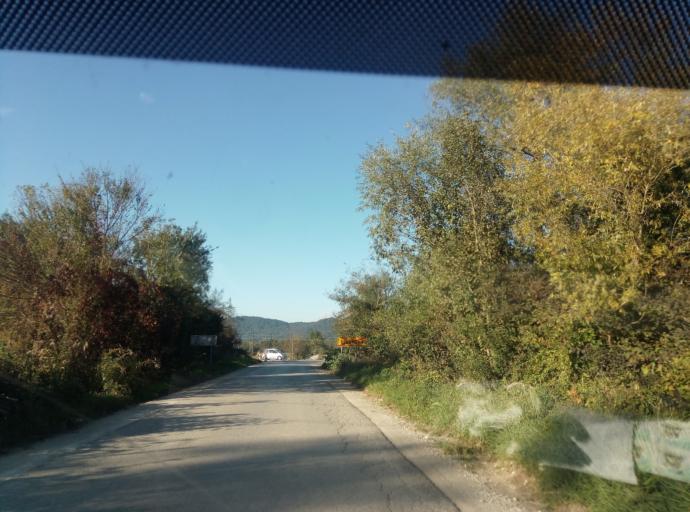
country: SI
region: Ljubljana
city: Ljubljana
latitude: 46.1018
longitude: 14.5029
